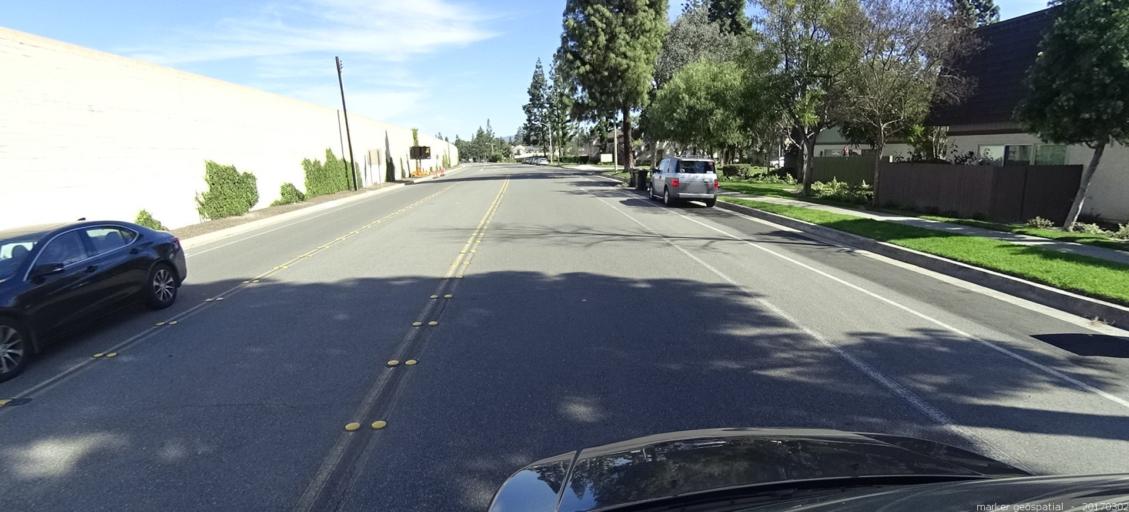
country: US
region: California
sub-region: Orange County
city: Placentia
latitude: 33.8463
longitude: -117.8680
